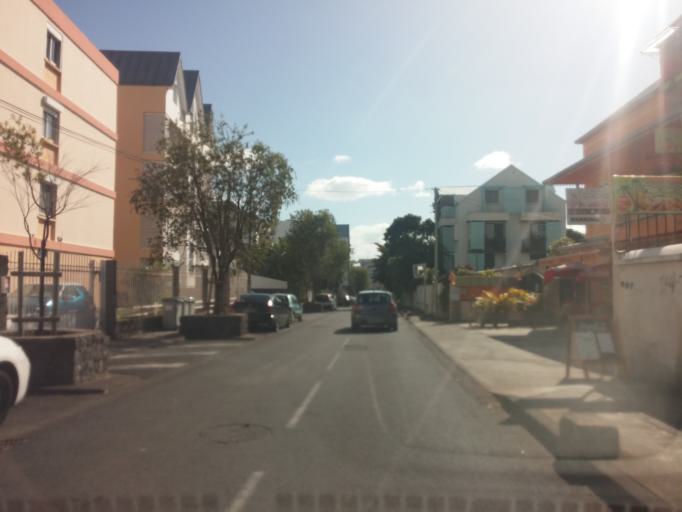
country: RE
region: Reunion
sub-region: Reunion
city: Saint-Denis
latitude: -20.8878
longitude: 55.4465
